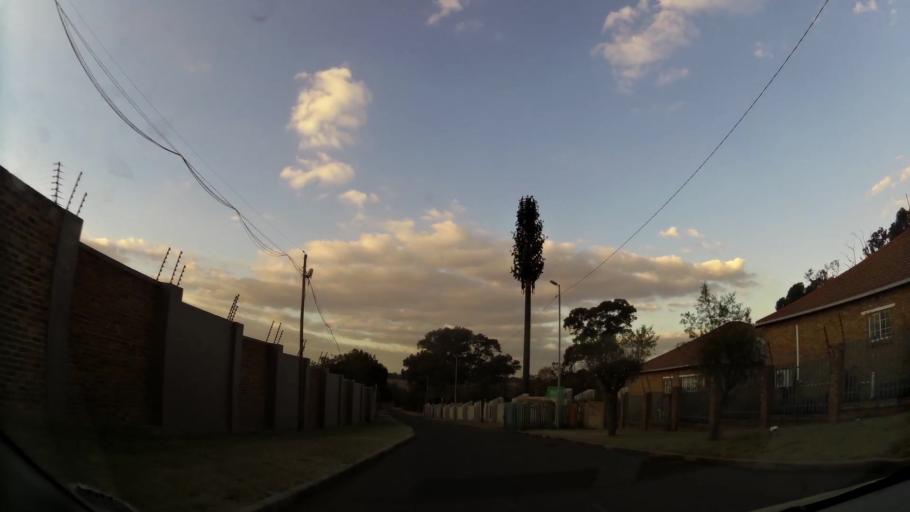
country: ZA
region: Gauteng
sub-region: West Rand District Municipality
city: Krugersdorp
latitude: -26.0677
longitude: 27.7940
